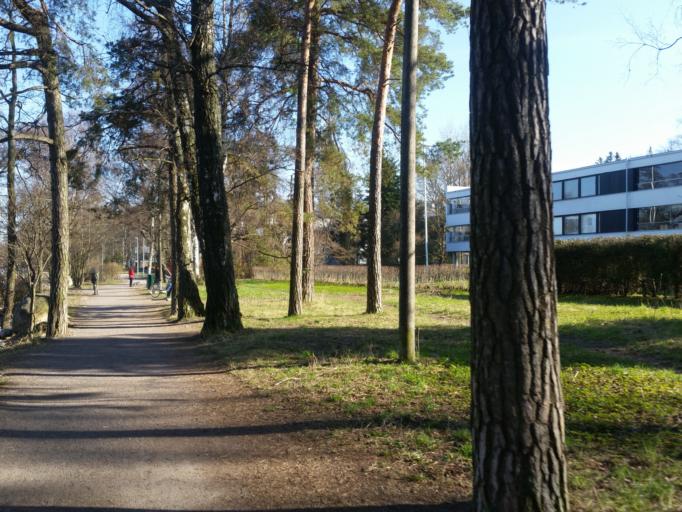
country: FI
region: Uusimaa
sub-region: Helsinki
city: Teekkarikylae
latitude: 60.1491
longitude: 24.8763
